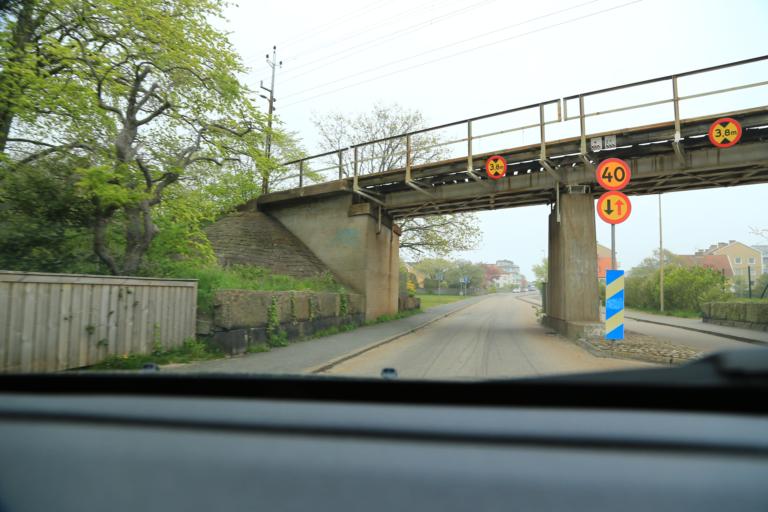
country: SE
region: Halland
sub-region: Varbergs Kommun
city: Varberg
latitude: 57.0992
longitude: 12.2452
